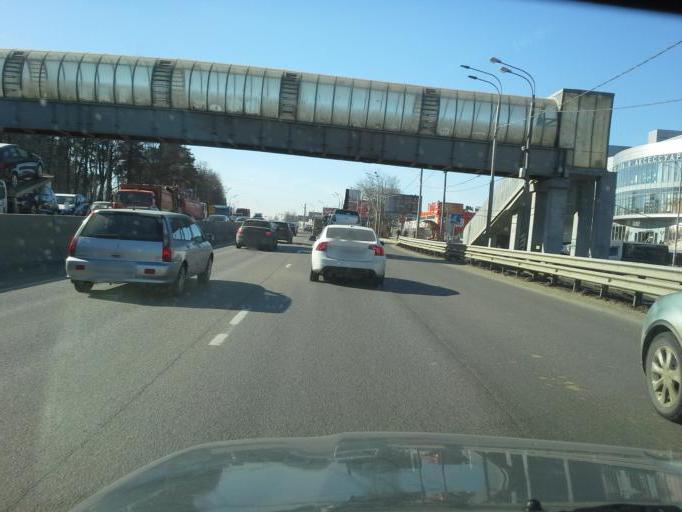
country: RU
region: Moskovskaya
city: Novoivanovskoye
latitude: 55.7090
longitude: 37.3635
